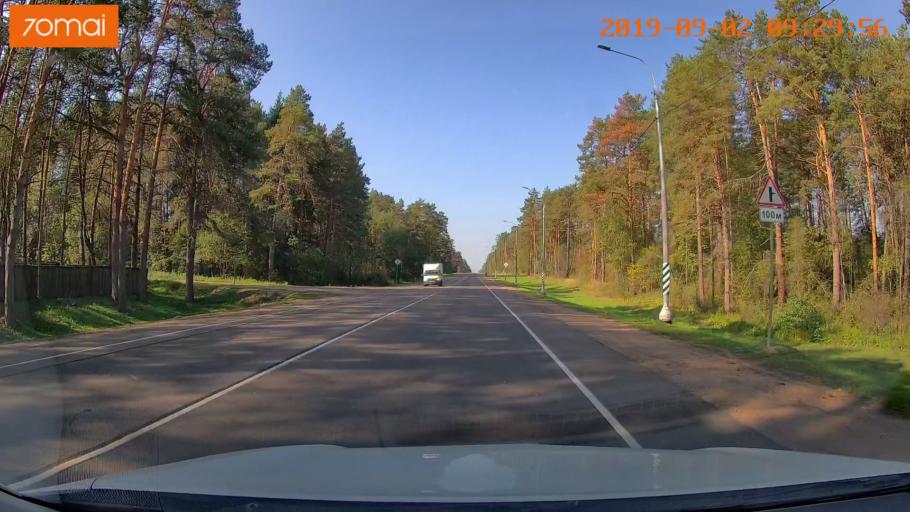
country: RU
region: Kaluga
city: Yukhnov
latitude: 54.7372
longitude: 35.2075
